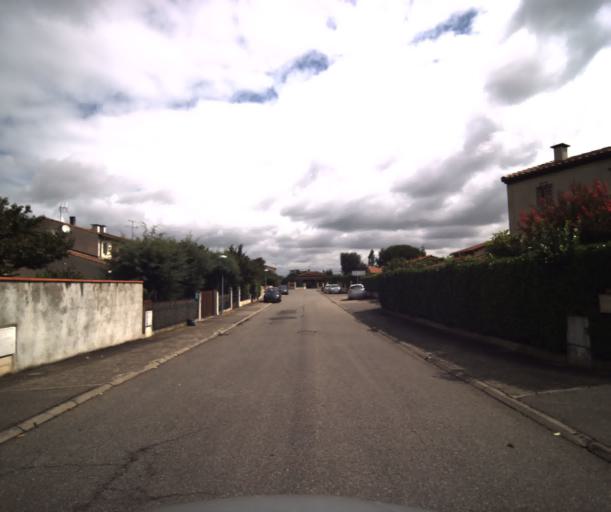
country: FR
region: Midi-Pyrenees
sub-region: Departement de la Haute-Garonne
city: Pinsaguel
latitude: 43.5178
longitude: 1.3940
